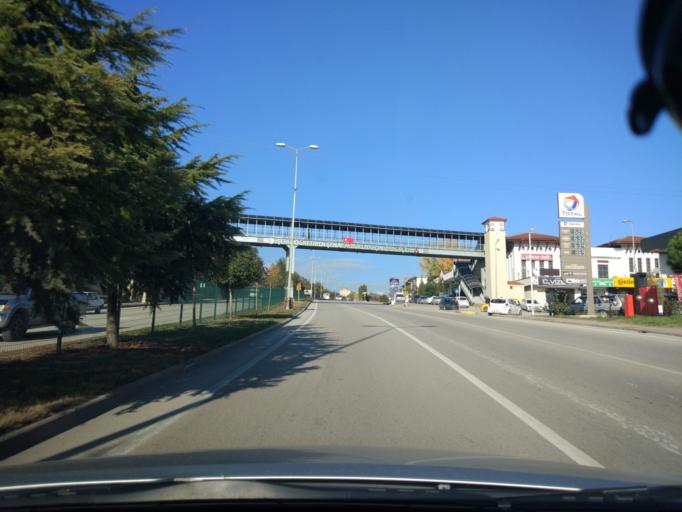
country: TR
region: Karabuk
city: Safranbolu
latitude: 41.2380
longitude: 32.6745
